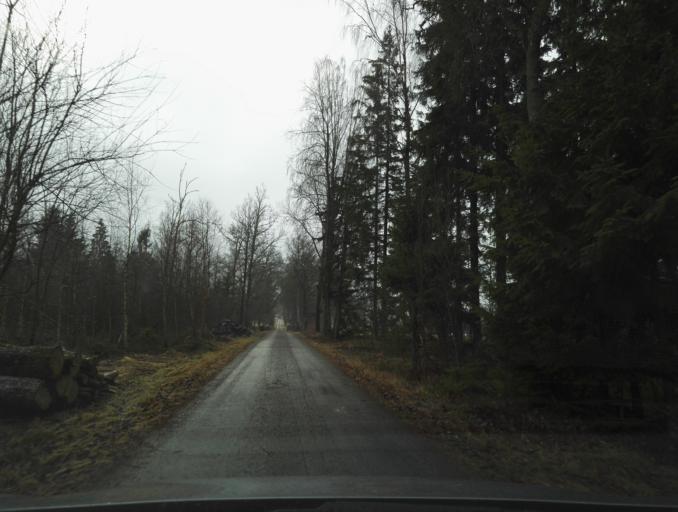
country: SE
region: Kronoberg
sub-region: Vaxjo Kommun
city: Vaexjoe
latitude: 56.9462
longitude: 14.7614
